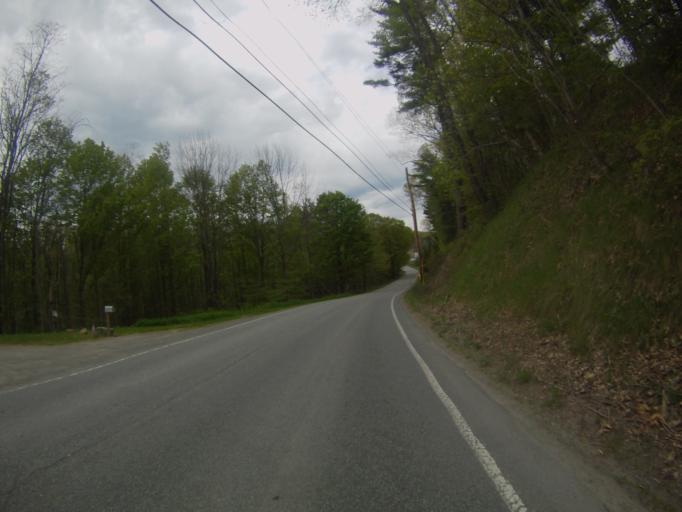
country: US
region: New York
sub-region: Essex County
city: Port Henry
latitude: 43.9575
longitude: -73.4870
